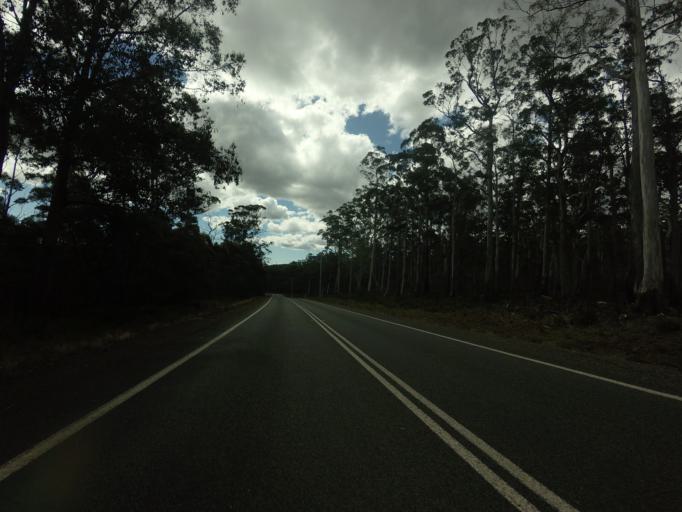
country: AU
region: Tasmania
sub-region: Northern Midlands
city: Evandale
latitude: -41.9945
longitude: 147.7150
